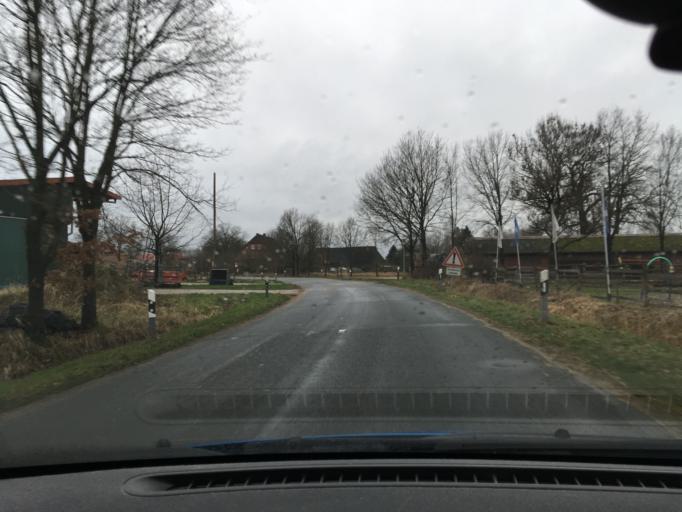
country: DE
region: Schleswig-Holstein
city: Lanze
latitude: 53.3672
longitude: 10.6344
